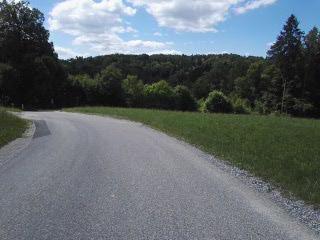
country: AT
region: Styria
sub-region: Politischer Bezirk Graz-Umgebung
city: Hart bei Graz
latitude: 47.0760
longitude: 15.5262
